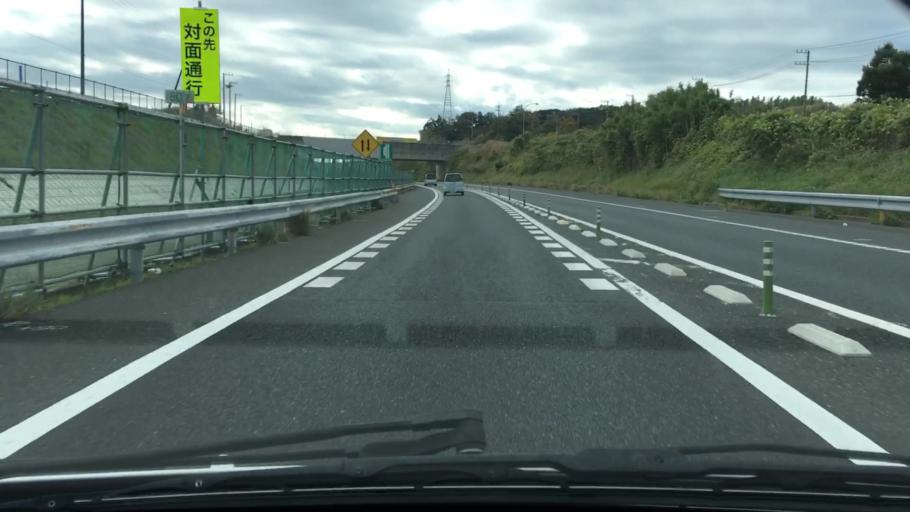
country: JP
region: Chiba
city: Kimitsu
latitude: 35.2426
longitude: 139.8889
